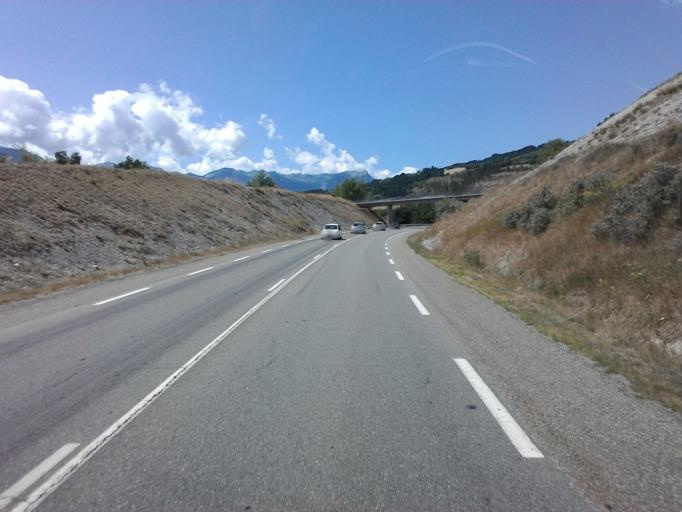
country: FR
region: Provence-Alpes-Cote d'Azur
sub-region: Departement des Hautes-Alpes
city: Embrun
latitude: 44.5935
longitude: 6.5193
